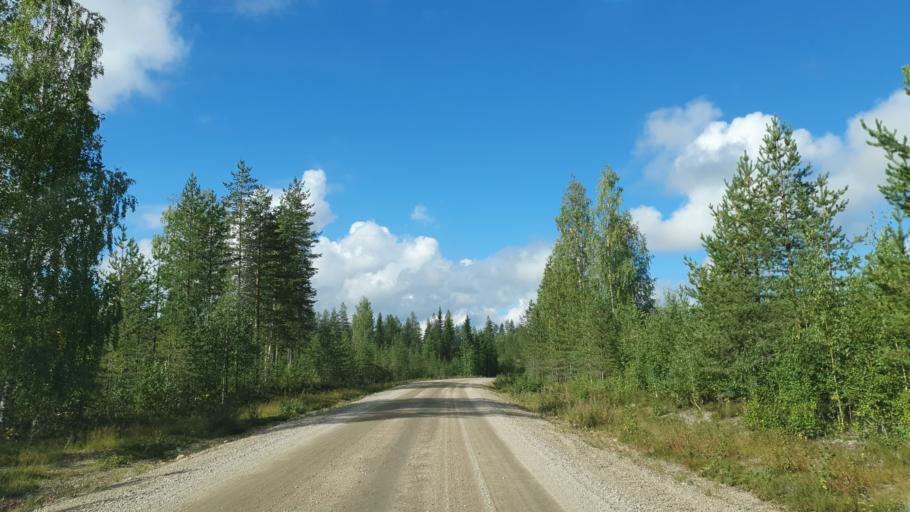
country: FI
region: Kainuu
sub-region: Kehys-Kainuu
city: Kuhmo
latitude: 63.9839
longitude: 29.2351
